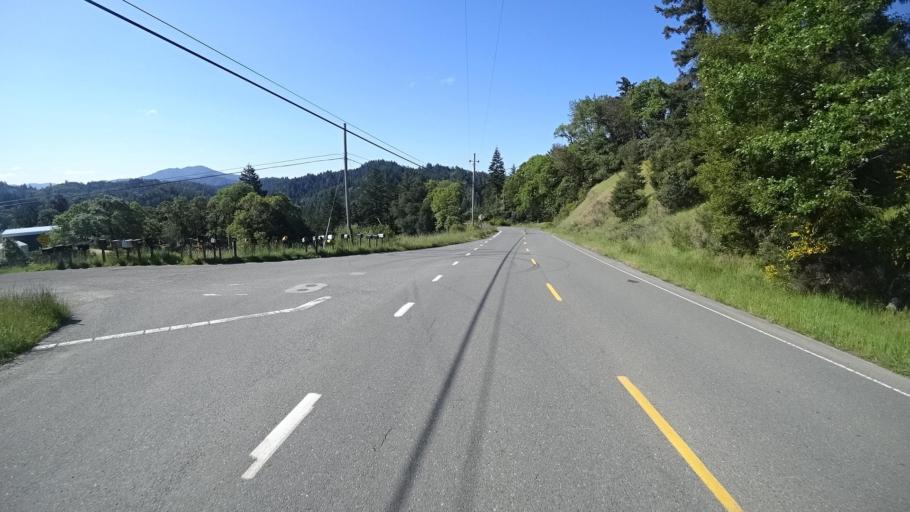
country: US
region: California
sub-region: Humboldt County
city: Redway
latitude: 40.1073
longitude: -123.7851
